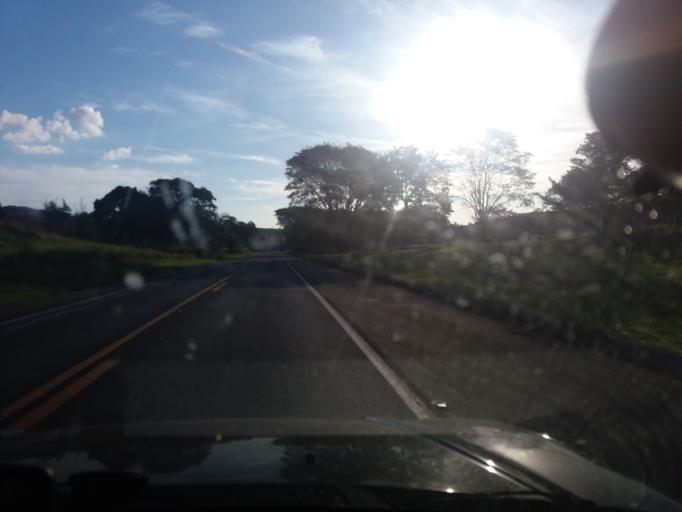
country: BR
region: Sao Paulo
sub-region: Buri
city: Buri
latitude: -23.9303
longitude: -48.6459
